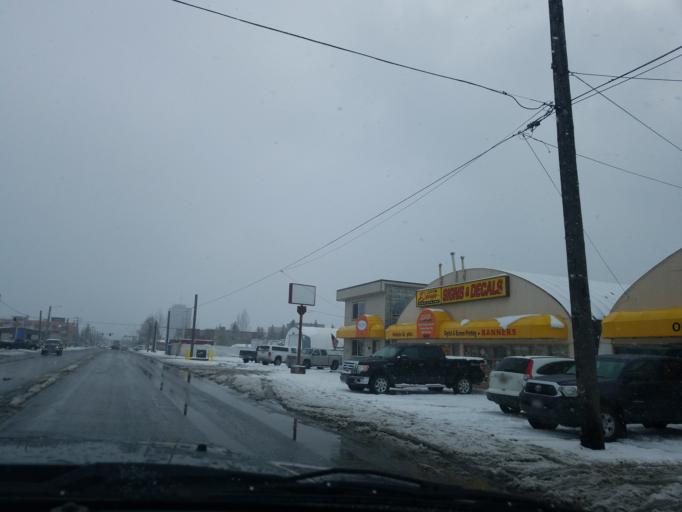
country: US
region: Alaska
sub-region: Anchorage Municipality
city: Anchorage
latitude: 61.1985
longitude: -149.8926
